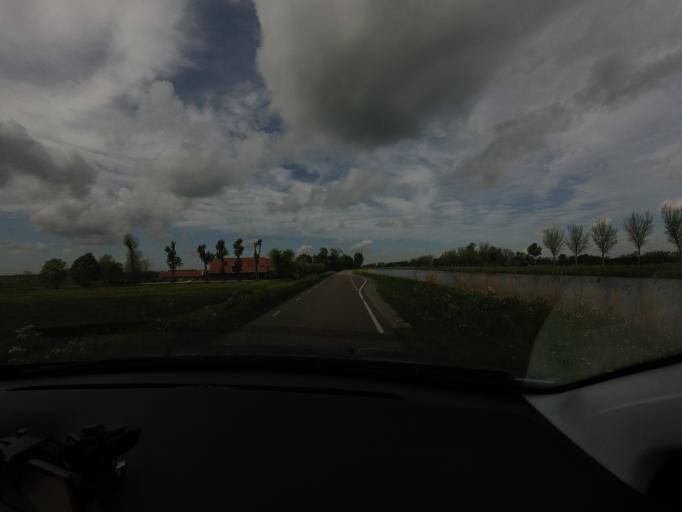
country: NL
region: North Holland
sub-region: Gemeente Beemster
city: Halfweg
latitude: 52.5177
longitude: 4.8907
